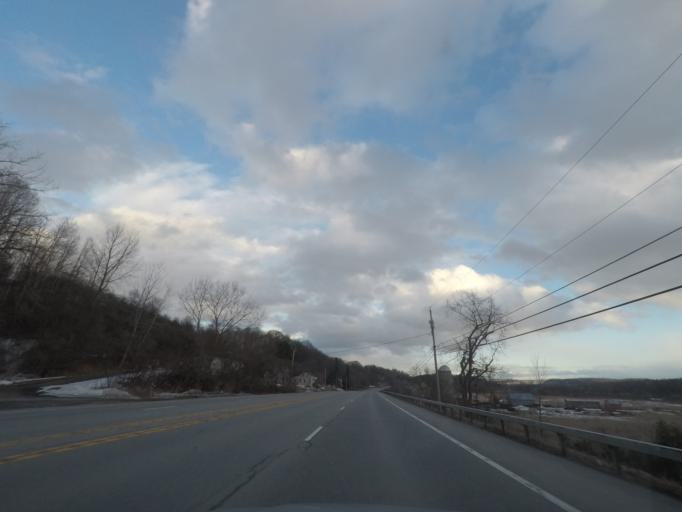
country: US
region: New York
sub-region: Herkimer County
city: Little Falls
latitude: 43.0334
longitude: -74.8049
